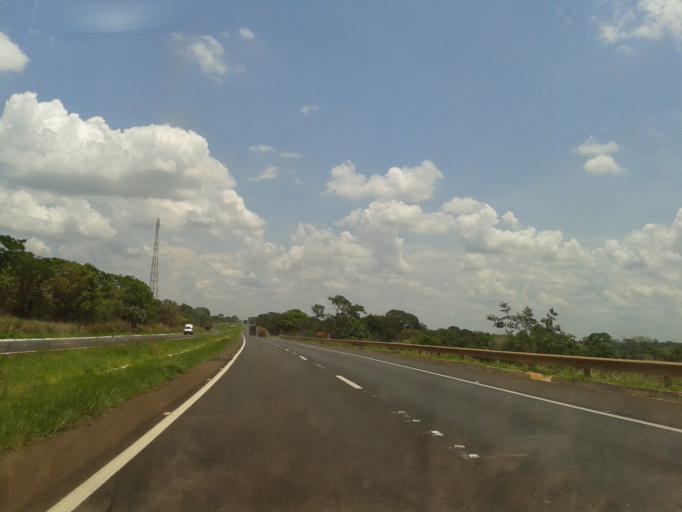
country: BR
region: Minas Gerais
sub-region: Monte Alegre De Minas
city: Monte Alegre de Minas
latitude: -18.8524
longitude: -48.7833
